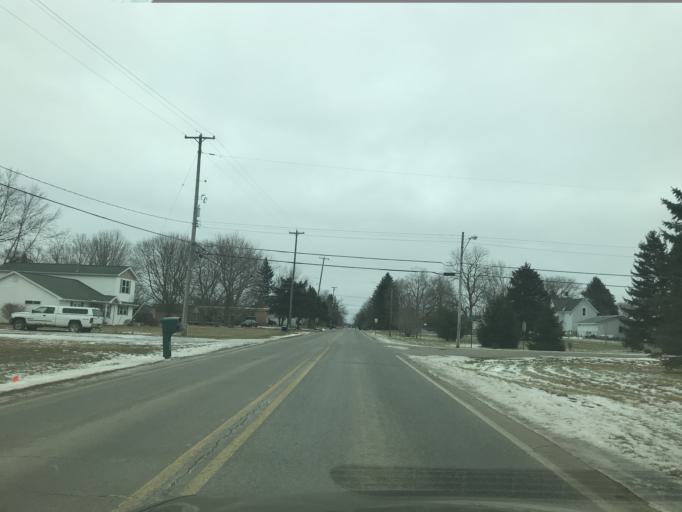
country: US
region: Michigan
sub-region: Jackson County
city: Brooklyn
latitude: 42.0734
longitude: -84.3322
